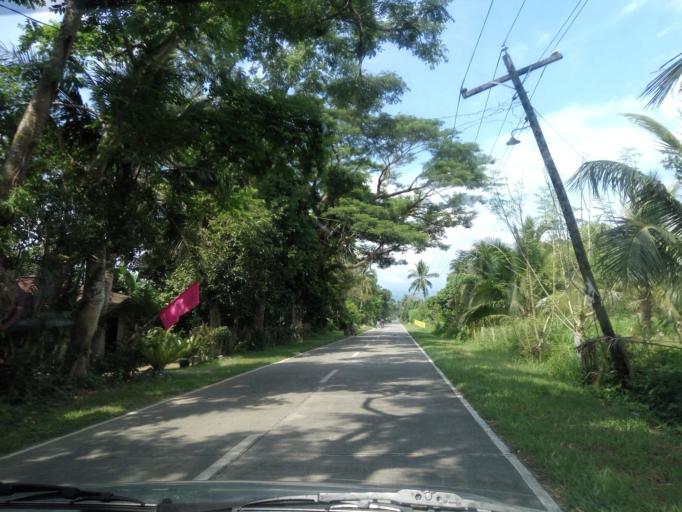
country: PH
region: Central Luzon
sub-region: Province of Aurora
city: Maria Aurora
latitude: 15.7935
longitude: 121.4523
